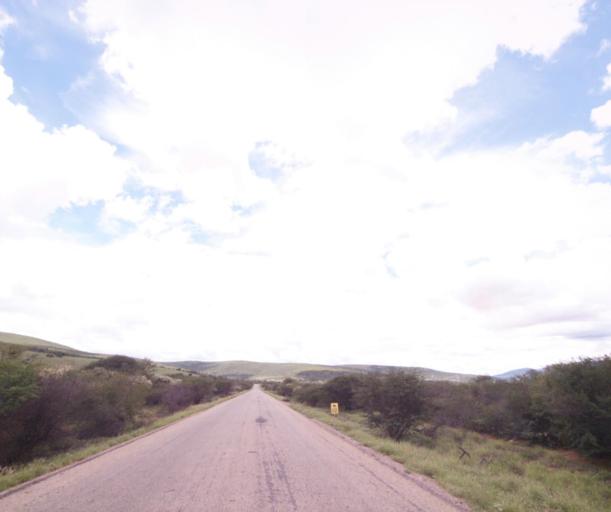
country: BR
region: Bahia
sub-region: Brumado
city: Brumado
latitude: -14.1886
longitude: -41.5758
